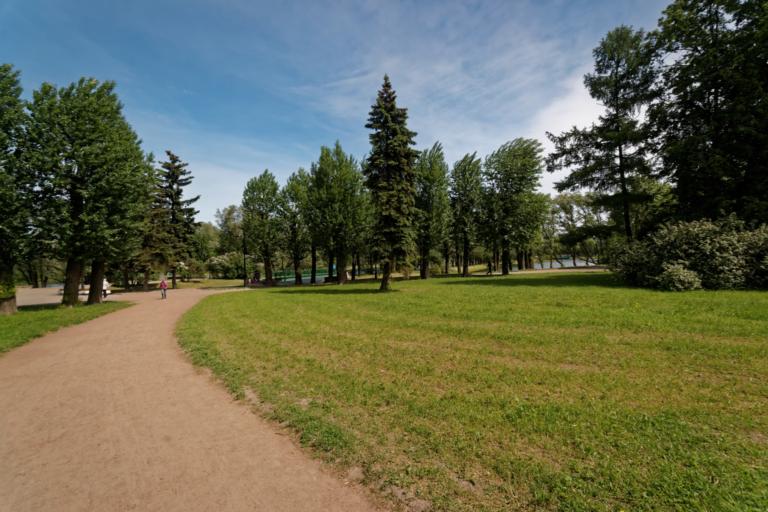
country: RU
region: St.-Petersburg
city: Kupchino
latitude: 59.8665
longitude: 30.3255
